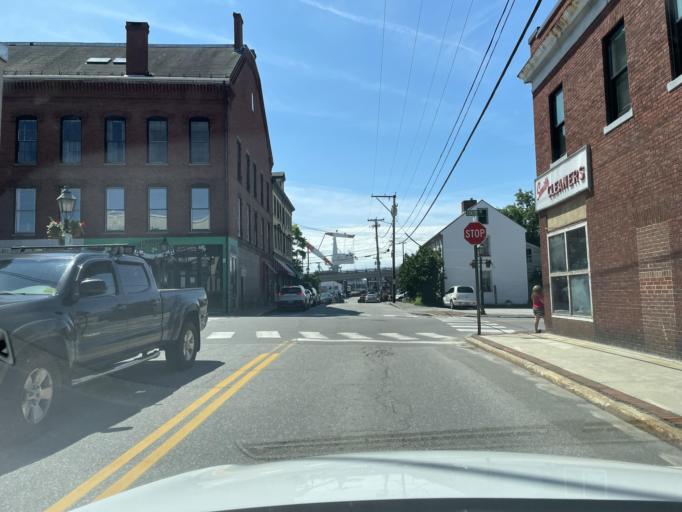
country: US
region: Maine
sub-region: Sagadahoc County
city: Bath
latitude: 43.9128
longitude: -69.8154
